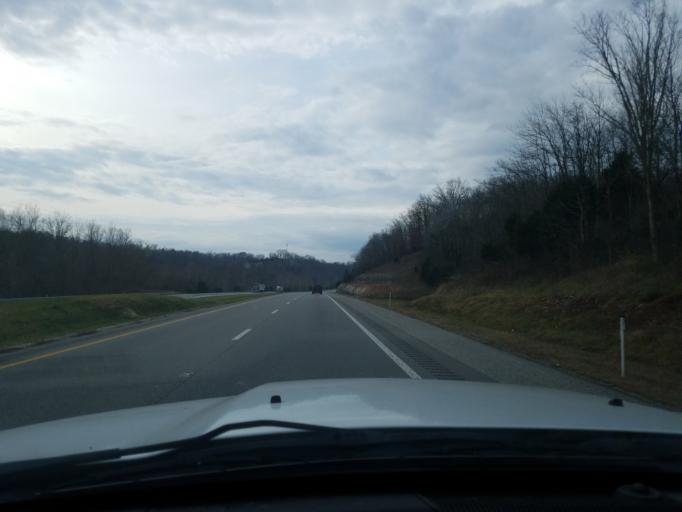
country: US
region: Kentucky
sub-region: Carter County
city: Olive Hill
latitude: 38.3227
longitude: -83.1628
